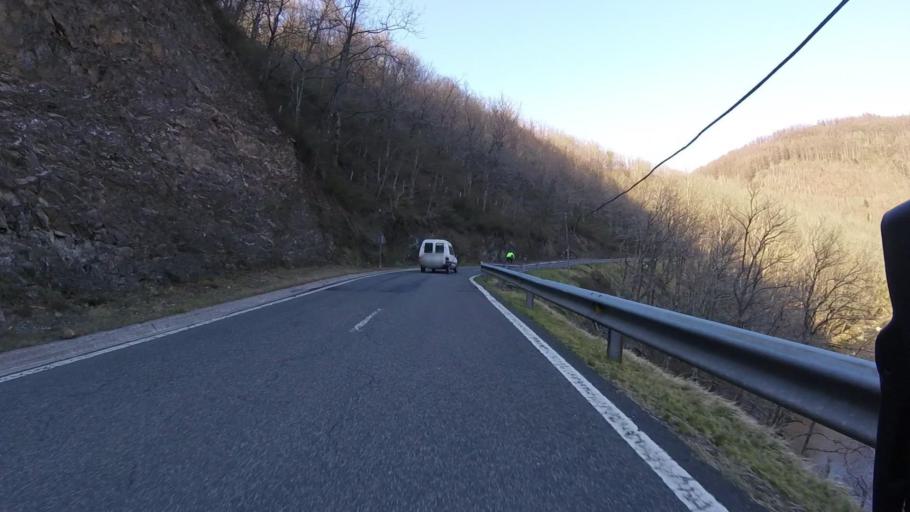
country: ES
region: Navarre
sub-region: Provincia de Navarra
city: Arano
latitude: 43.2091
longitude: -1.8626
